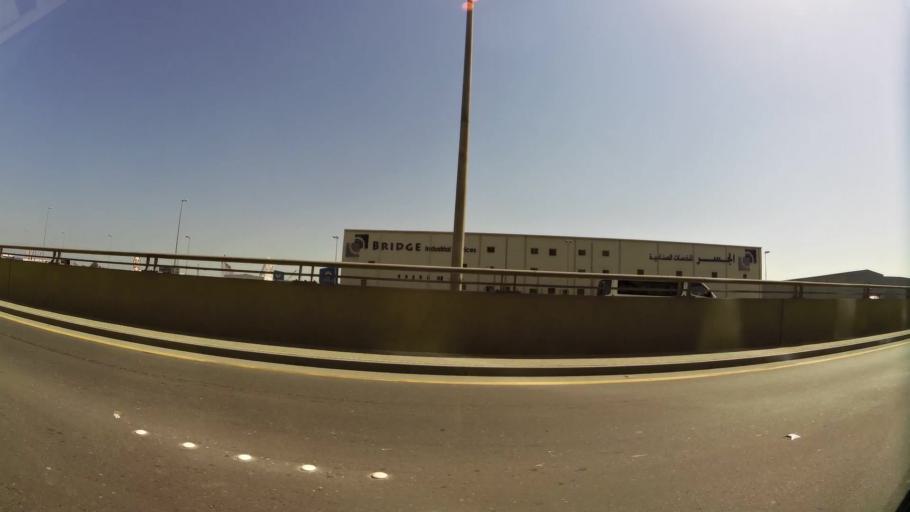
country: BH
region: Manama
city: Manama
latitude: 26.2018
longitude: 50.5987
